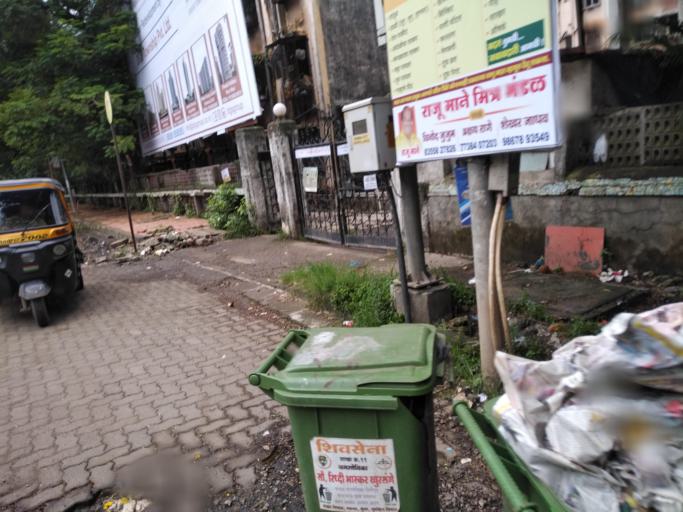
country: IN
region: Maharashtra
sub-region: Mumbai Suburban
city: Borivli
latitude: 19.2388
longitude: 72.8645
